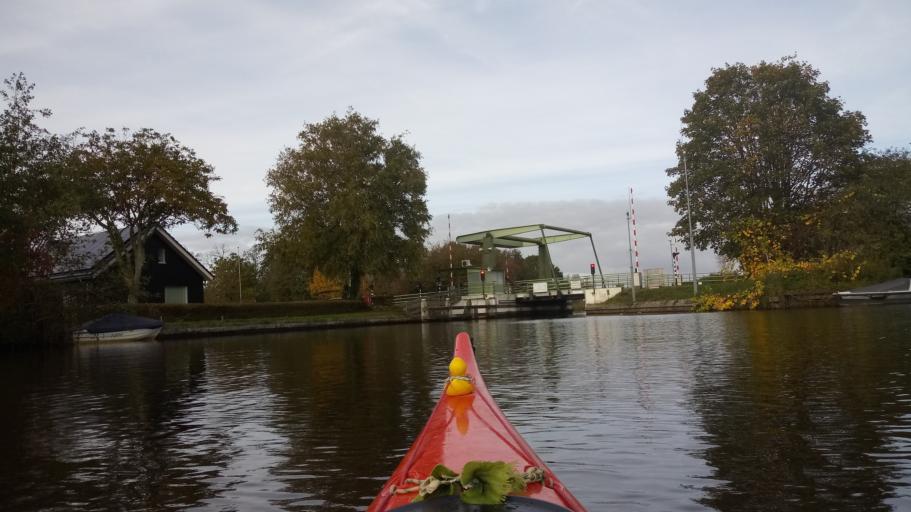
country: NL
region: Overijssel
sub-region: Gemeente Steenwijkerland
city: Sint Jansklooster
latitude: 52.6874
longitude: 6.0453
